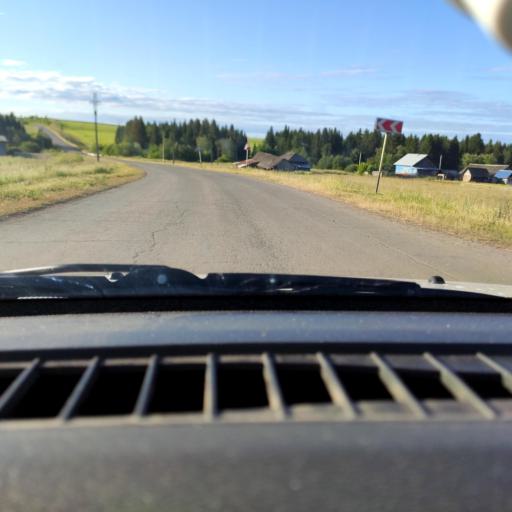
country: RU
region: Perm
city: Uinskoye
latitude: 57.0739
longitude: 56.5601
